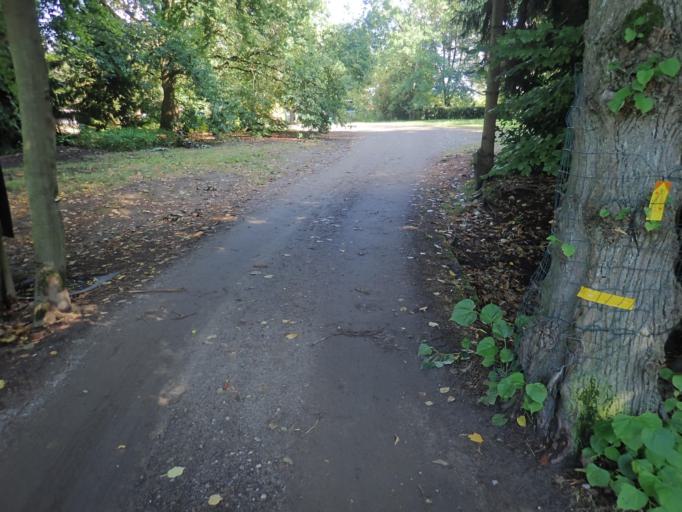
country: BE
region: Flanders
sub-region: Provincie Vlaams-Brabant
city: Keerbergen
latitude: 51.0290
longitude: 4.6628
